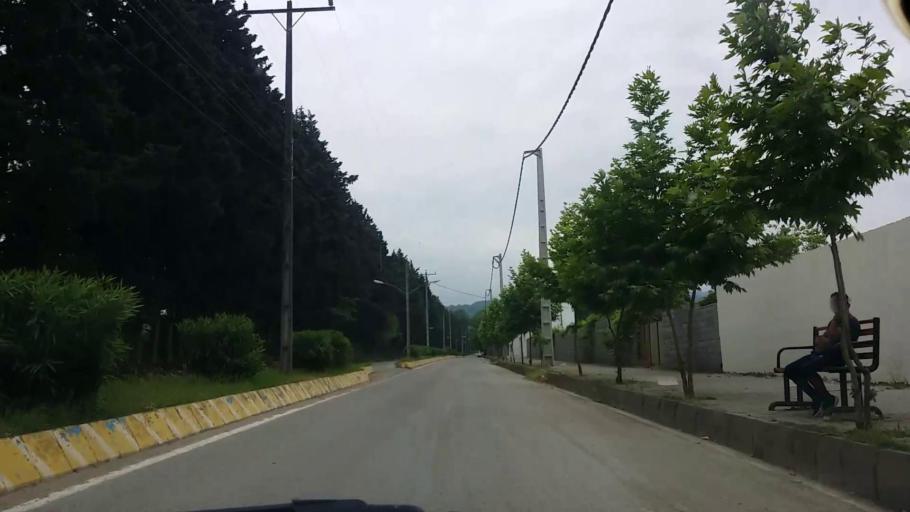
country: IR
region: Mazandaran
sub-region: Nowshahr
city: Nowshahr
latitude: 36.6359
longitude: 51.5024
